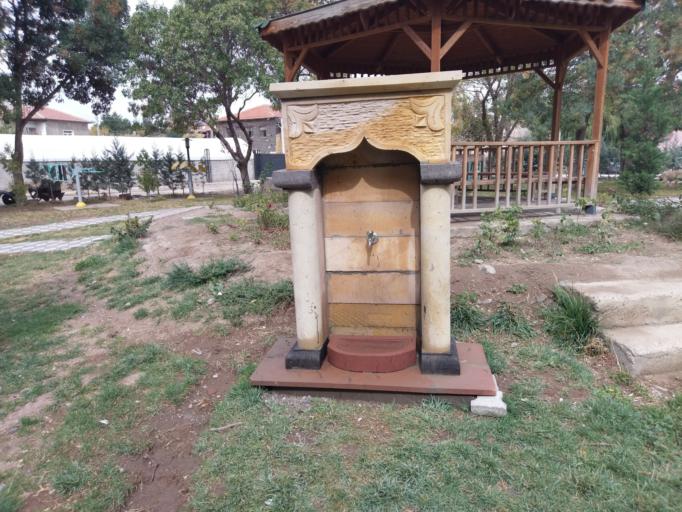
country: TR
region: Kayseri
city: Tomarza
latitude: 38.4476
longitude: 35.8030
